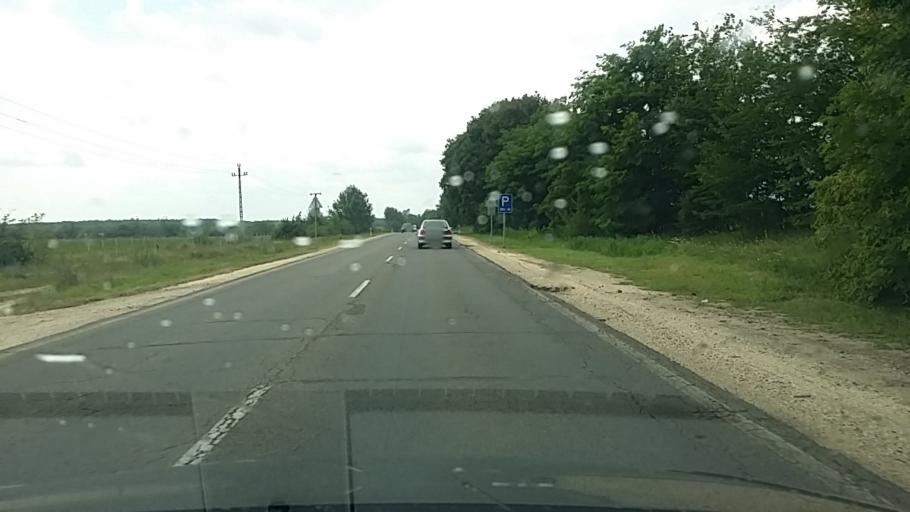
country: HU
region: Pest
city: Orkeny
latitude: 47.1355
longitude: 19.4116
